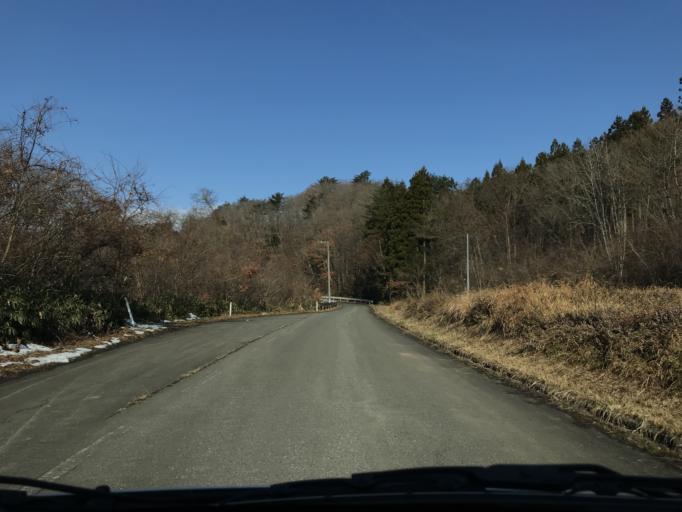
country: JP
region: Iwate
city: Ichinoseki
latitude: 38.9694
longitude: 141.0435
